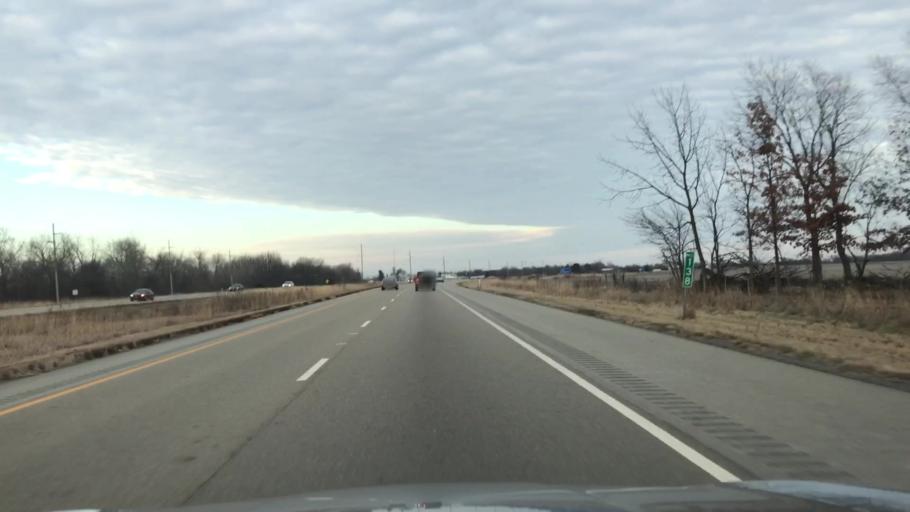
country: US
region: Illinois
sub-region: Logan County
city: Atlanta
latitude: 40.2463
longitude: -89.2486
